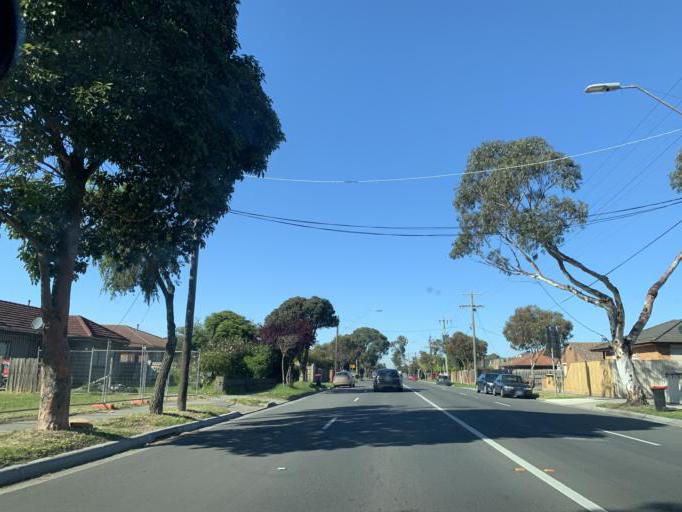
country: AU
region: Victoria
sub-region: Greater Dandenong
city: Dandenong
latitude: -37.9953
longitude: 145.2095
